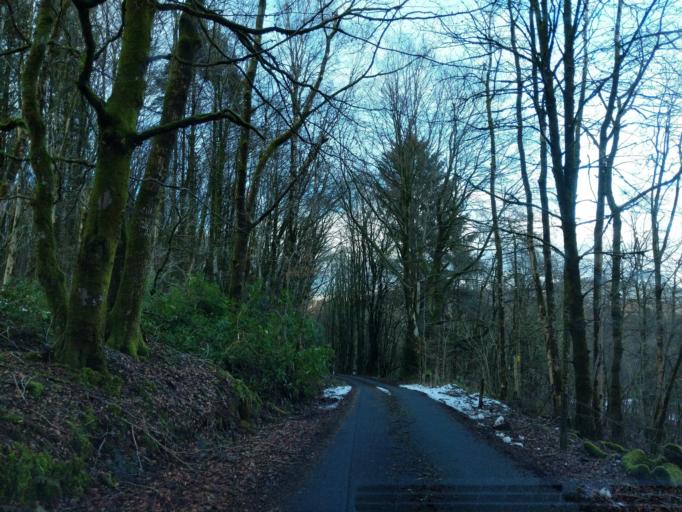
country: GB
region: Scotland
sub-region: Dumfries and Galloway
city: Moffat
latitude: 55.3225
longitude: -3.4754
